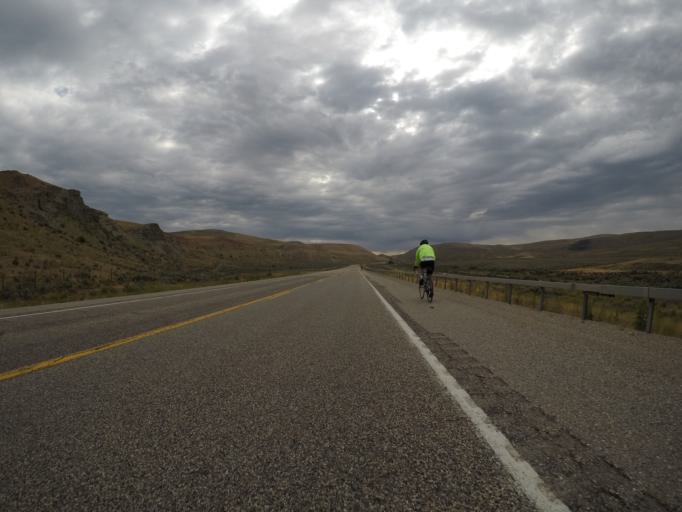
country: US
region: Utah
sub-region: Rich County
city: Randolph
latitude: 41.8221
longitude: -110.8851
